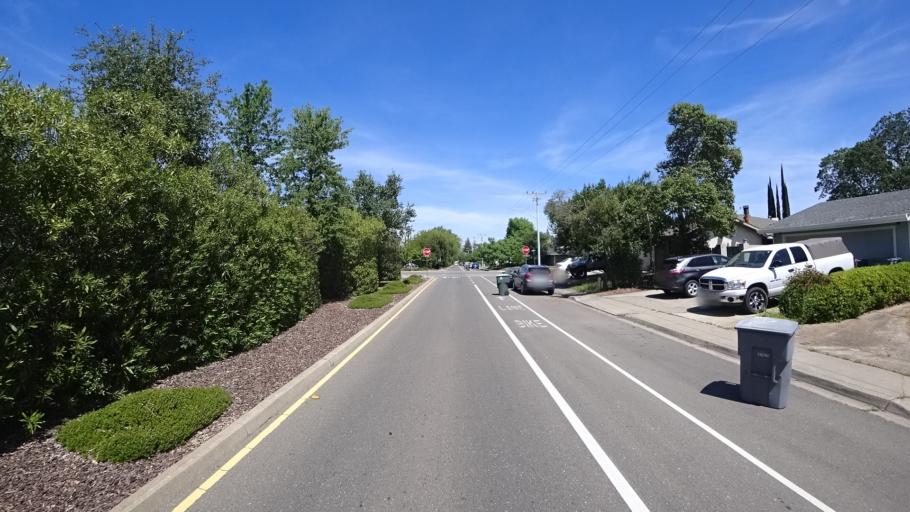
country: US
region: California
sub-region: Placer County
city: Rocklin
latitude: 38.7821
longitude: -121.2574
